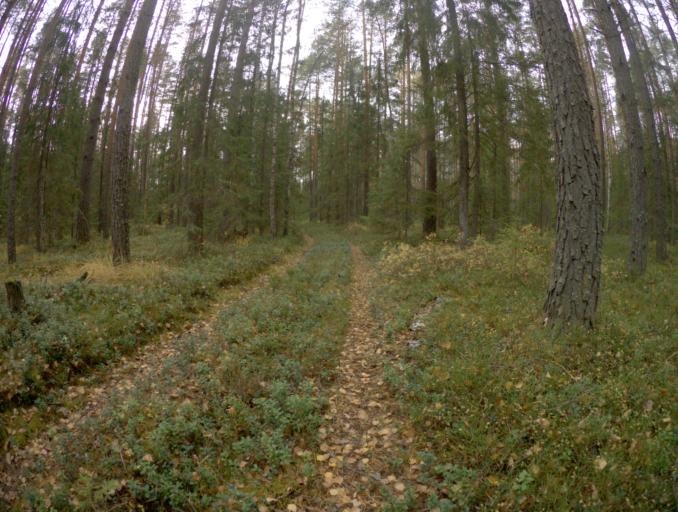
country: RU
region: Vladimir
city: Raduzhnyy
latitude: 55.9299
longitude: 40.3369
